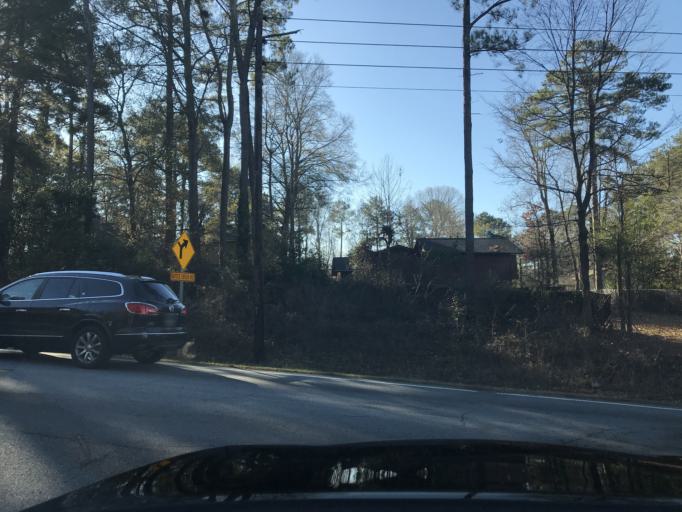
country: US
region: Georgia
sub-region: Clayton County
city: Riverdale
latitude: 33.5564
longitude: -84.3757
